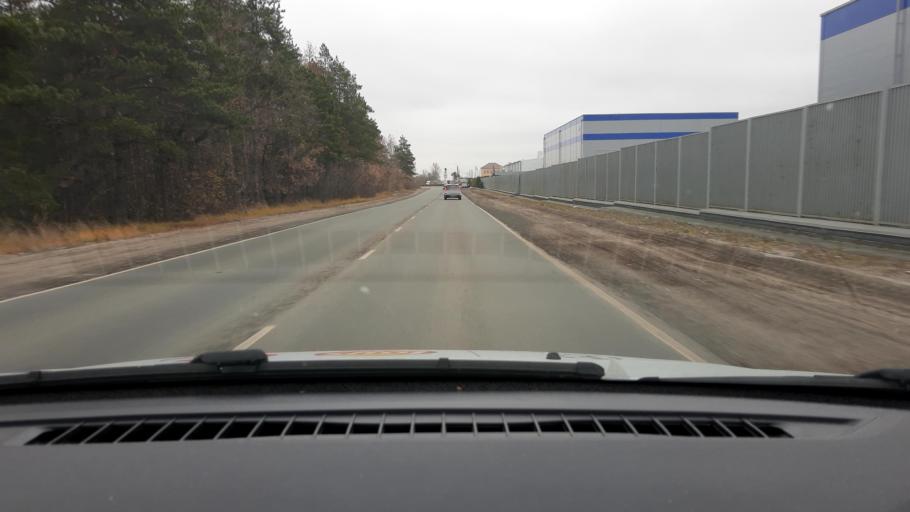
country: RU
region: Nizjnij Novgorod
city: Dzerzhinsk
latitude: 56.2587
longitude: 43.4618
